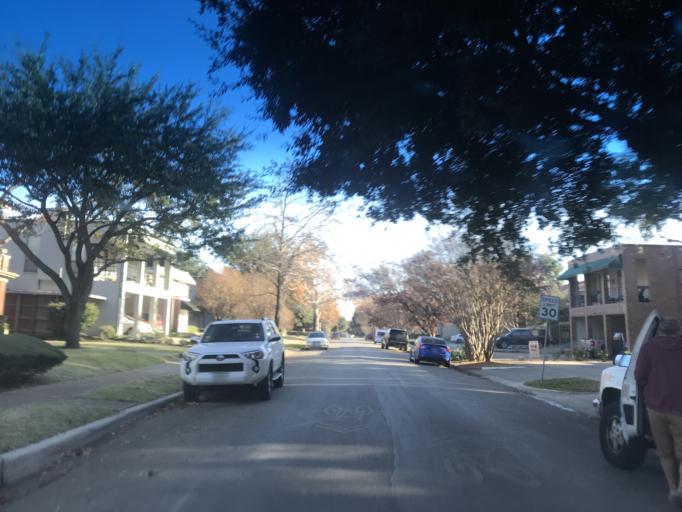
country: US
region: Texas
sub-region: Dallas County
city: Highland Park
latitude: 32.8165
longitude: -96.8072
